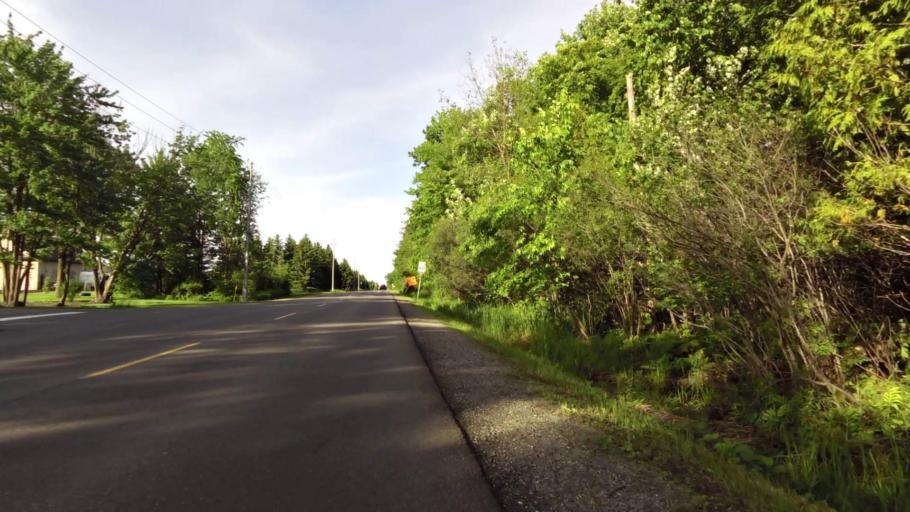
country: CA
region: Ontario
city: Ottawa
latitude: 45.2440
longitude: -75.6030
